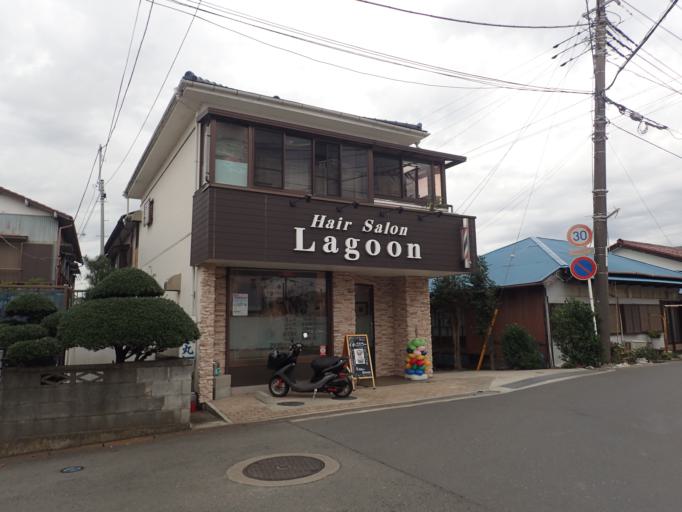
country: JP
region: Kanagawa
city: Miura
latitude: 35.1591
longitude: 139.6279
